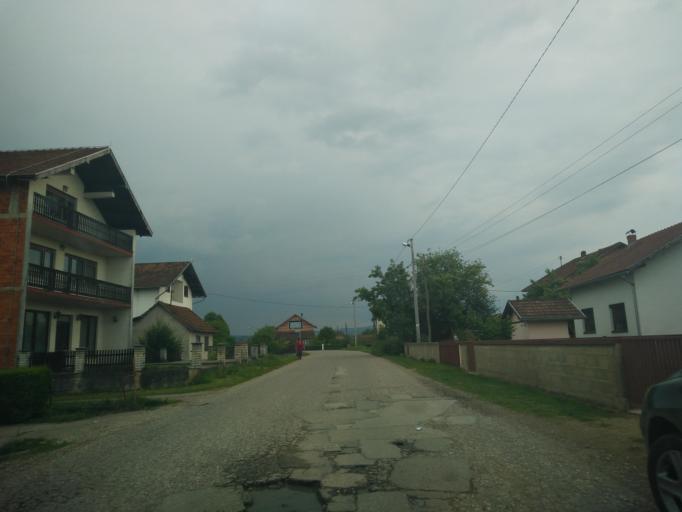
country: BA
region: Republika Srpska
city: Prijedor
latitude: 44.9469
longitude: 16.7022
